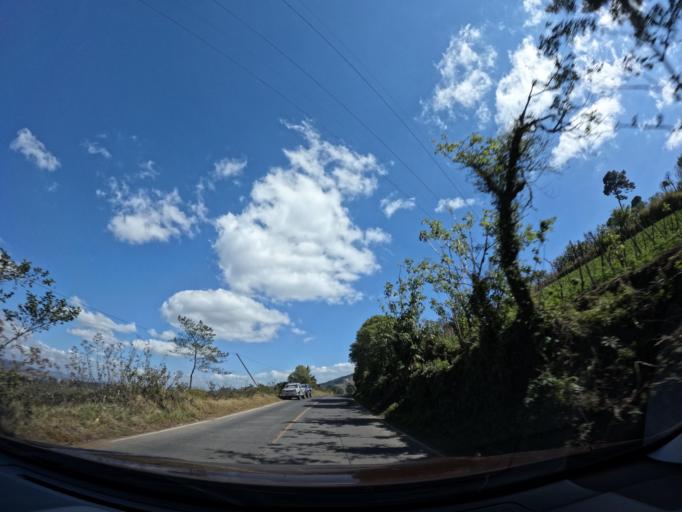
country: GT
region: Chimaltenango
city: Patzun
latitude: 14.6485
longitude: -91.0440
